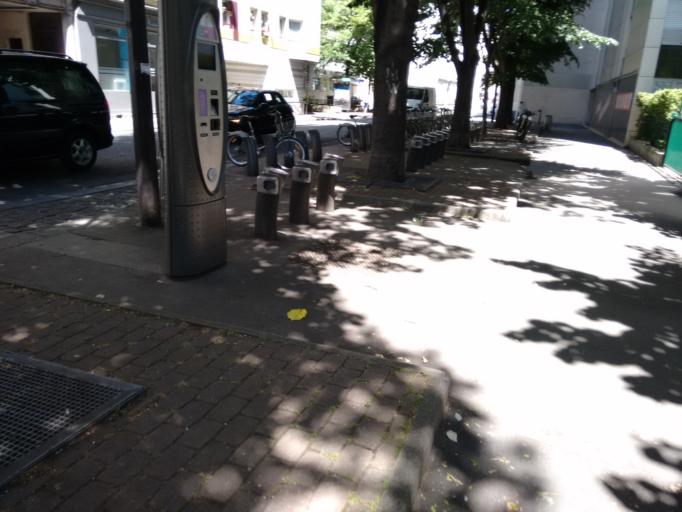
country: FR
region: Ile-de-France
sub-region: Departement des Hauts-de-Seine
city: Malakoff
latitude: 48.8366
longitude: 2.3070
